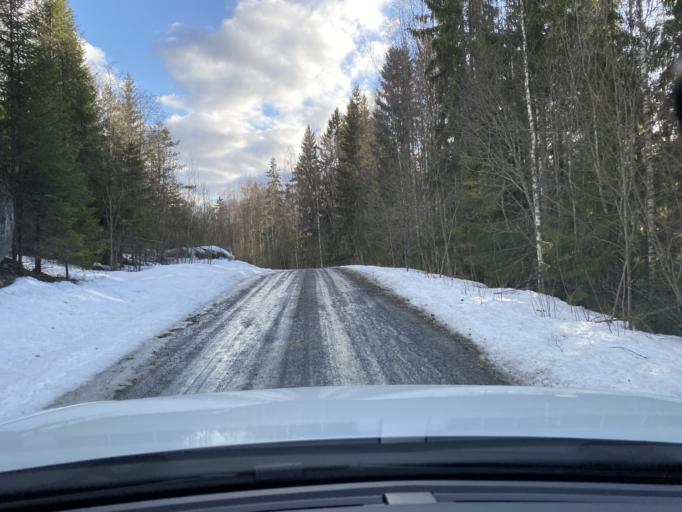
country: FI
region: Pirkanmaa
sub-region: Lounais-Pirkanmaa
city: Mouhijaervi
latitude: 61.4526
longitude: 22.9595
